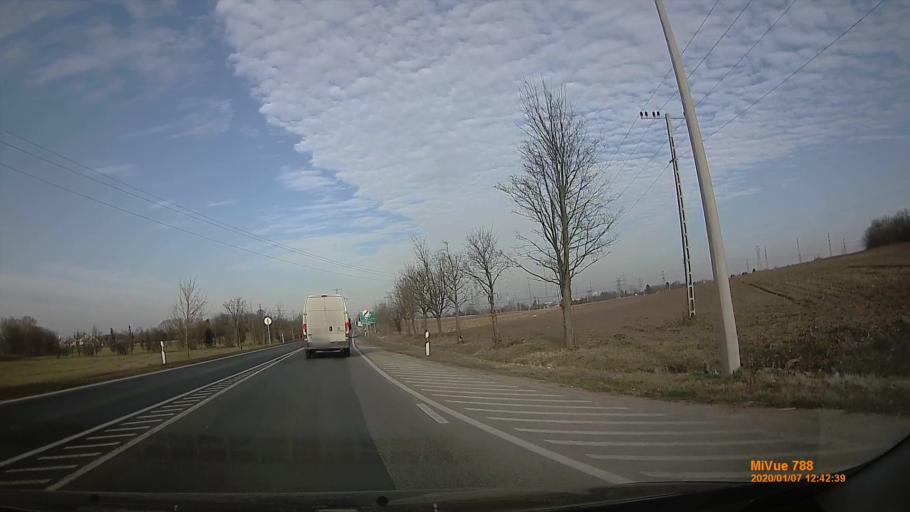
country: HU
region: Gyor-Moson-Sopron
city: Gyor
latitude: 47.6630
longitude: 17.6892
